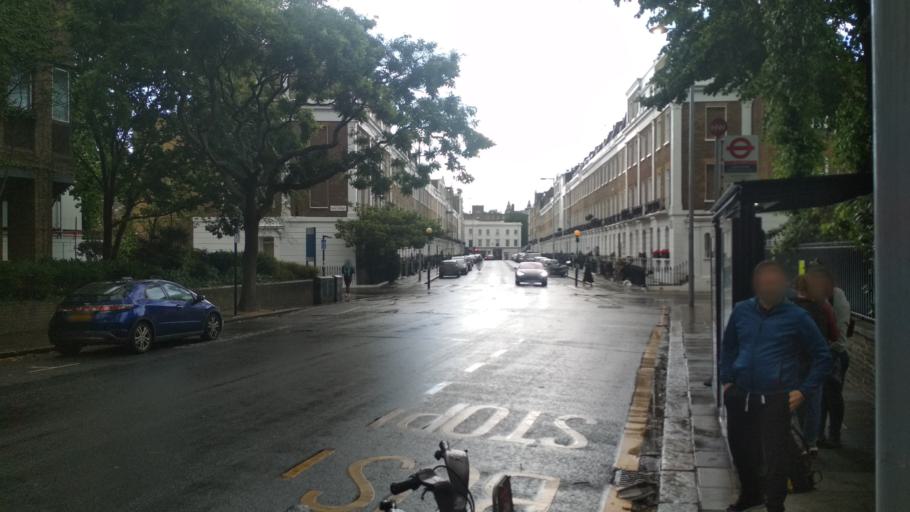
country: GB
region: England
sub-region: Greater London
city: Chelsea
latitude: 51.4898
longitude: -0.1703
